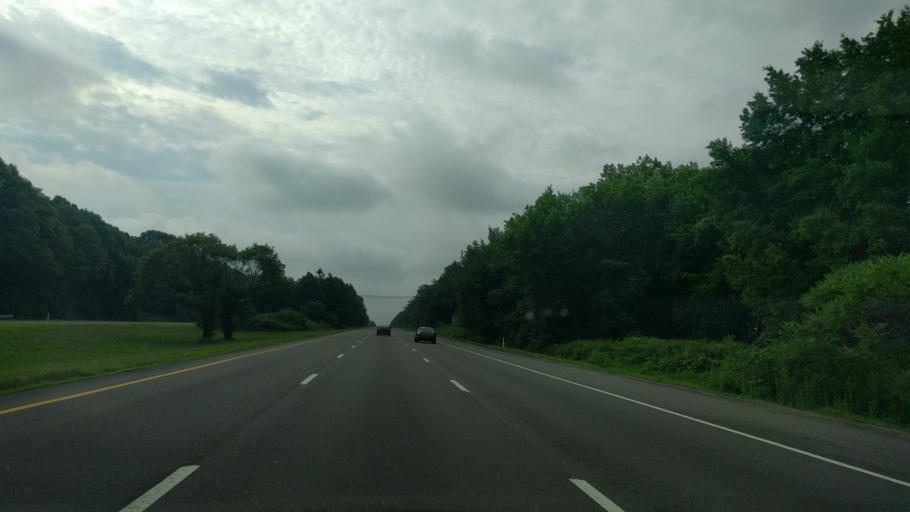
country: US
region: Massachusetts
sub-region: Bristol County
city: Seekonk
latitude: 41.8004
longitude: -71.3273
